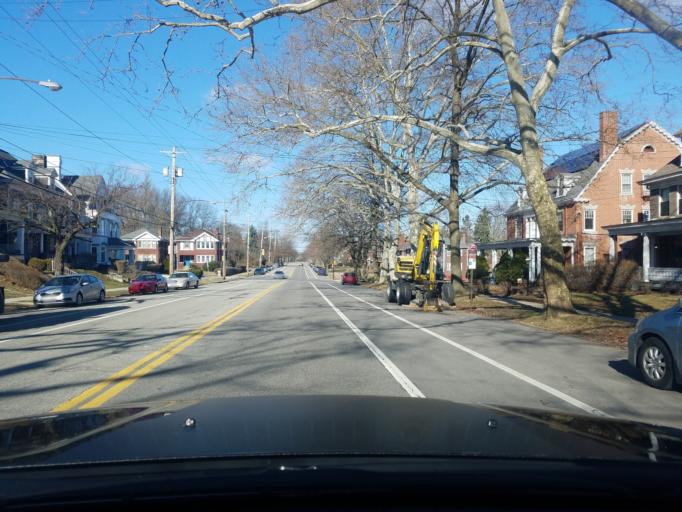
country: US
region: Pennsylvania
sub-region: Allegheny County
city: Wilkinsburg
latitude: 40.4506
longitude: -79.8991
